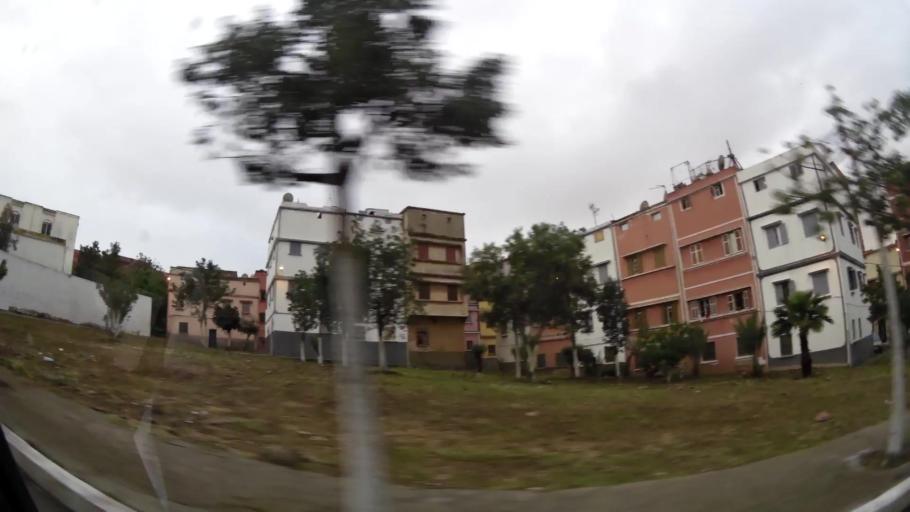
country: MA
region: Grand Casablanca
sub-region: Casablanca
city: Casablanca
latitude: 33.5544
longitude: -7.5833
